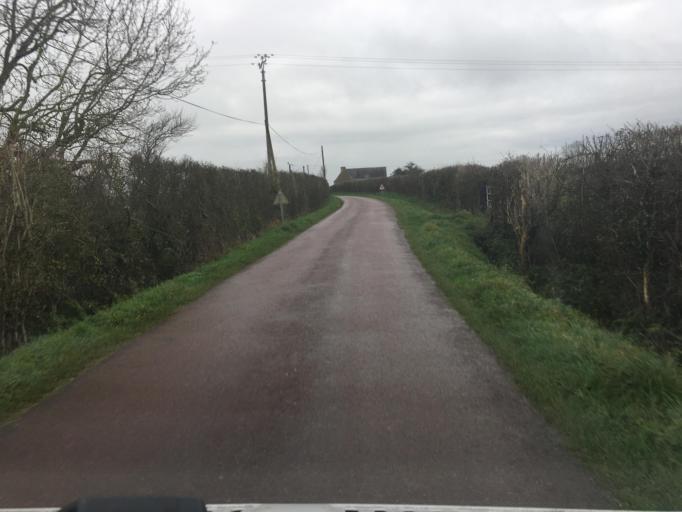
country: FR
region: Lower Normandy
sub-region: Departement de la Manche
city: Sainte-Mere-Eglise
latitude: 49.4389
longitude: -1.2550
